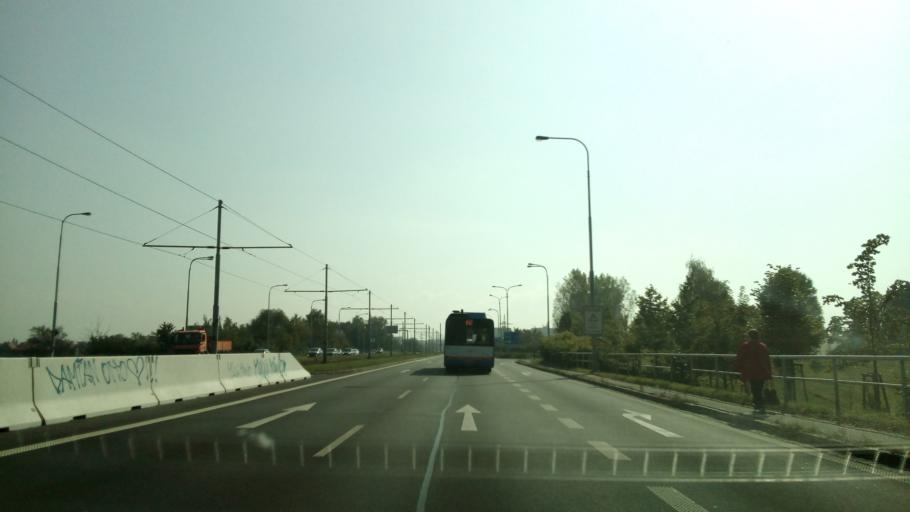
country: CZ
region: Moravskoslezsky
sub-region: Okres Ostrava-Mesto
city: Ostrava
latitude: 49.8007
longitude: 18.2466
